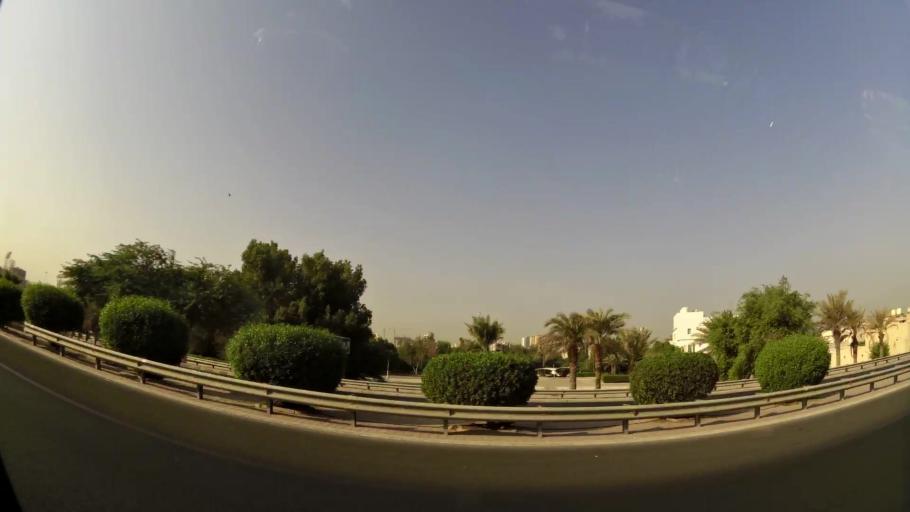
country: KW
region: Muhafazat Hawalli
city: Hawalli
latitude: 29.3455
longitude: 48.0315
